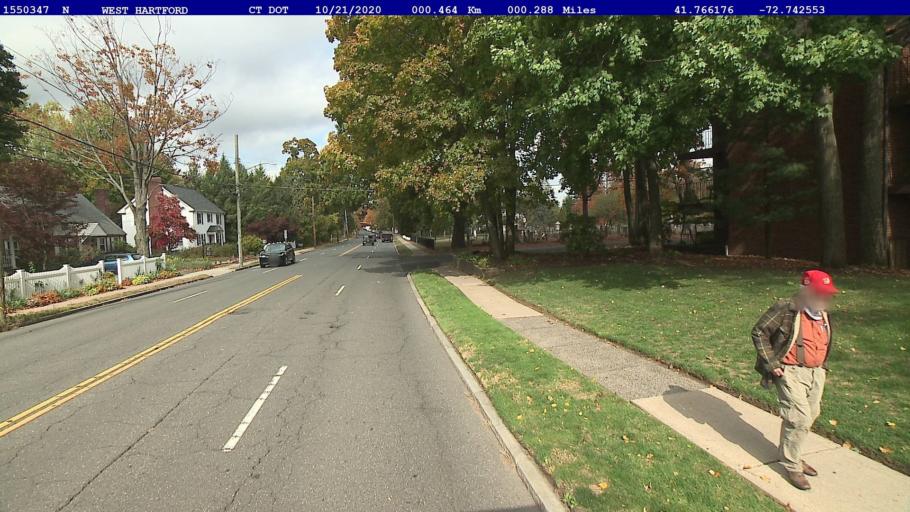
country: US
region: Connecticut
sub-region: Hartford County
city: West Hartford
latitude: 41.7662
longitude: -72.7426
